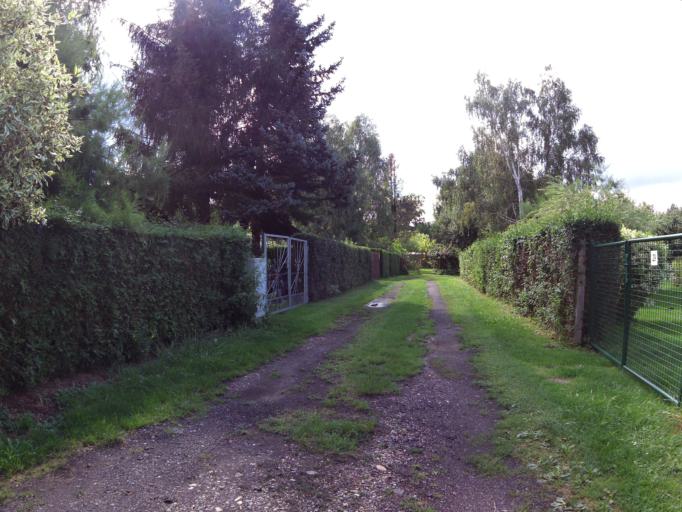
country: DE
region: Brandenburg
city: Storkow
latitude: 52.2594
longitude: 13.9300
